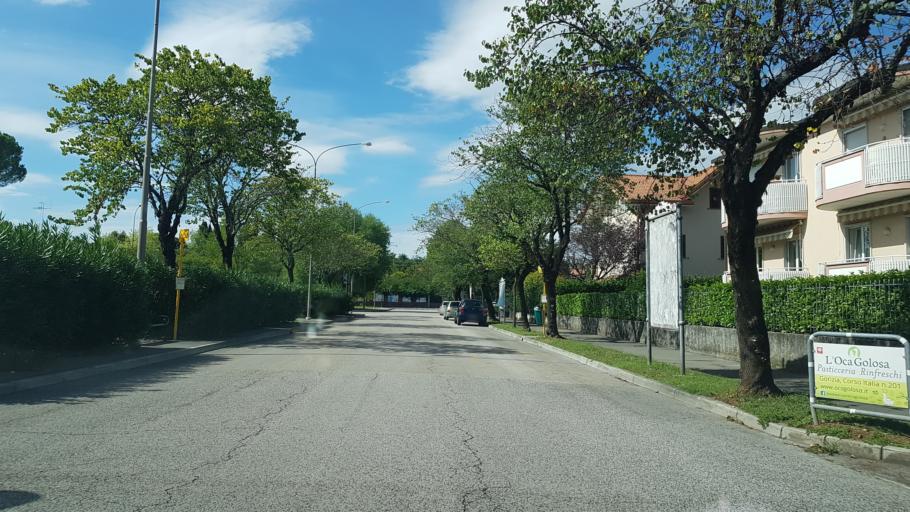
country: IT
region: Friuli Venezia Giulia
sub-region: Provincia di Gorizia
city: Gorizia
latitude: 45.9319
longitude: 13.6198
